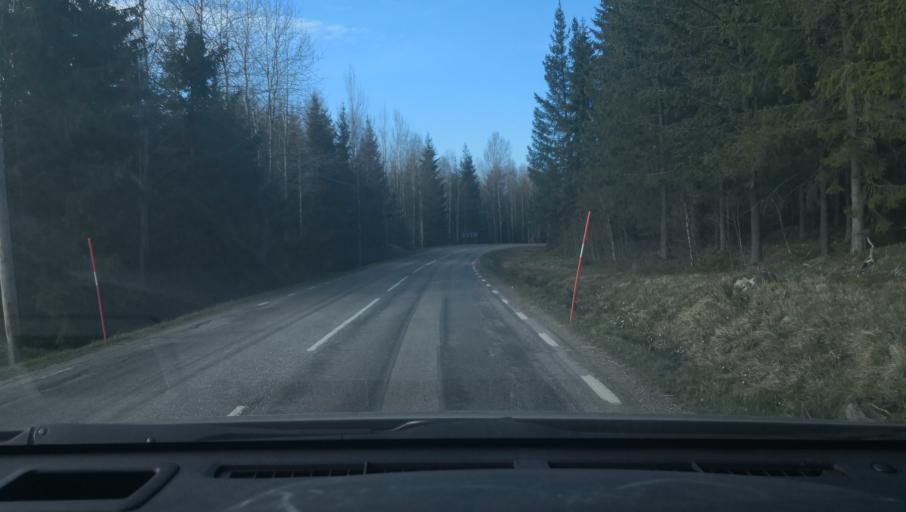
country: SE
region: Uppsala
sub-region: Heby Kommun
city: Heby
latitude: 59.9675
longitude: 16.8939
